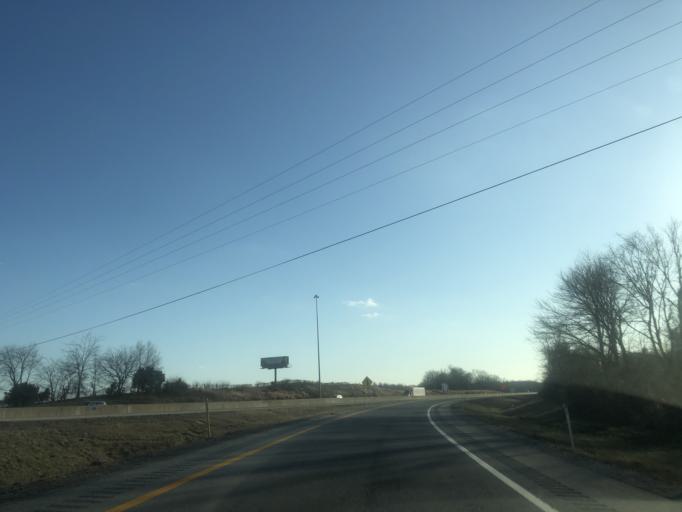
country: US
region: Kentucky
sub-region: Simpson County
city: Franklin
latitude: 36.6639
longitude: -86.5581
